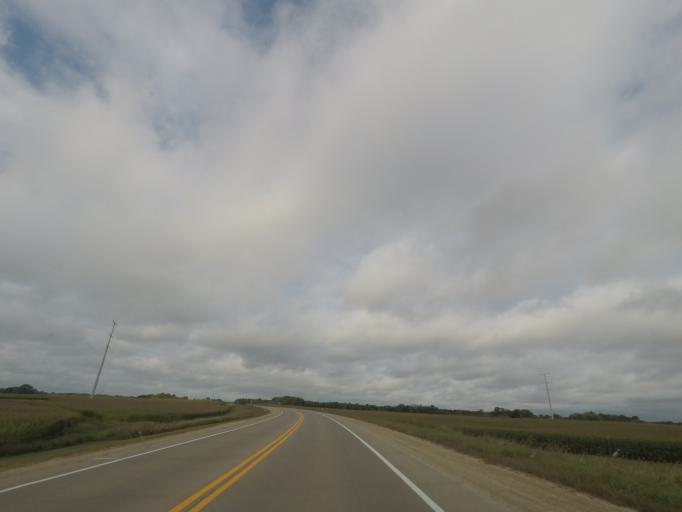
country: US
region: Wisconsin
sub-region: Jefferson County
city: Cambridge
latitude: 43.0188
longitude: -89.0390
